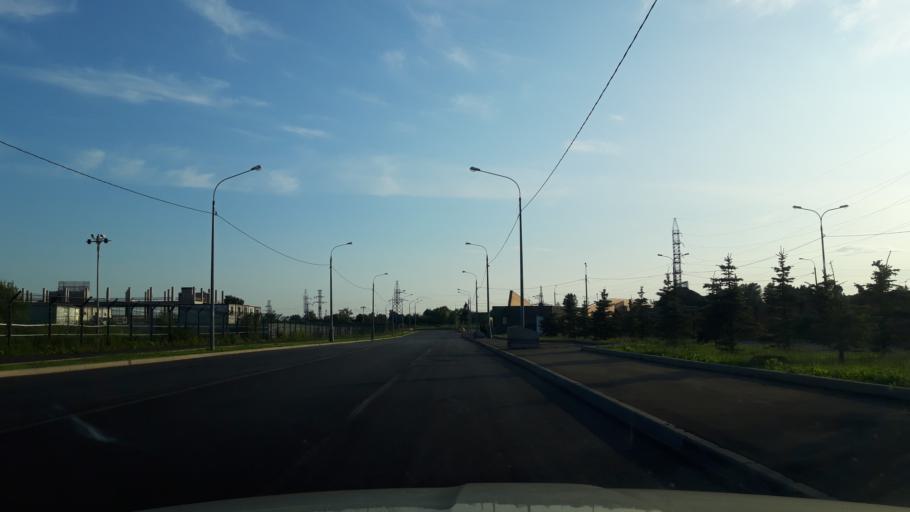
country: RU
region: Moskovskaya
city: Alabushevo
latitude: 56.0131
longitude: 37.1434
